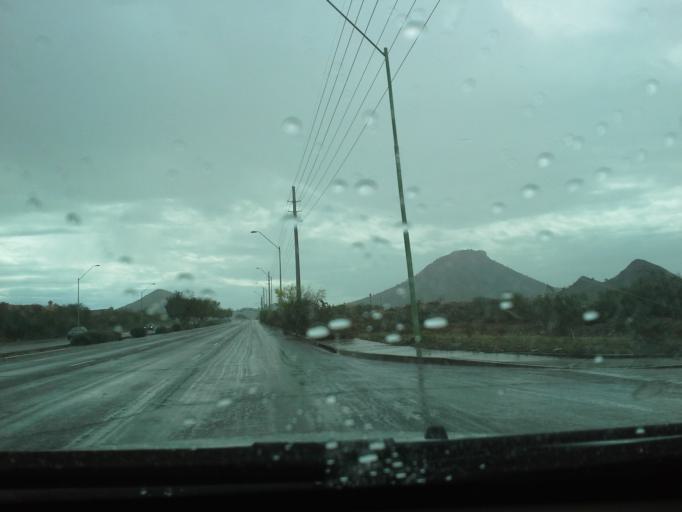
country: US
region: Arizona
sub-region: Maricopa County
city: Fountain Hills
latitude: 33.5823
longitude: -111.8050
